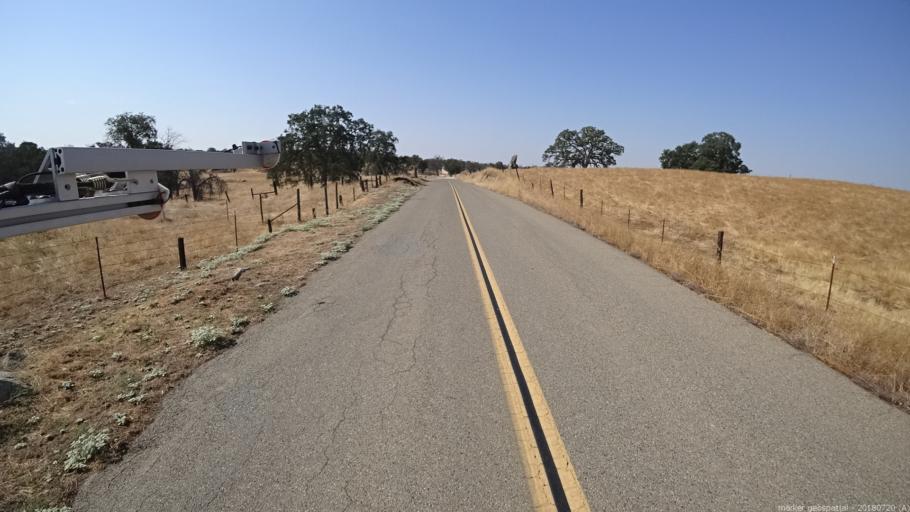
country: US
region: California
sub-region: Madera County
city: Yosemite Lakes
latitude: 37.2357
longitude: -119.9204
